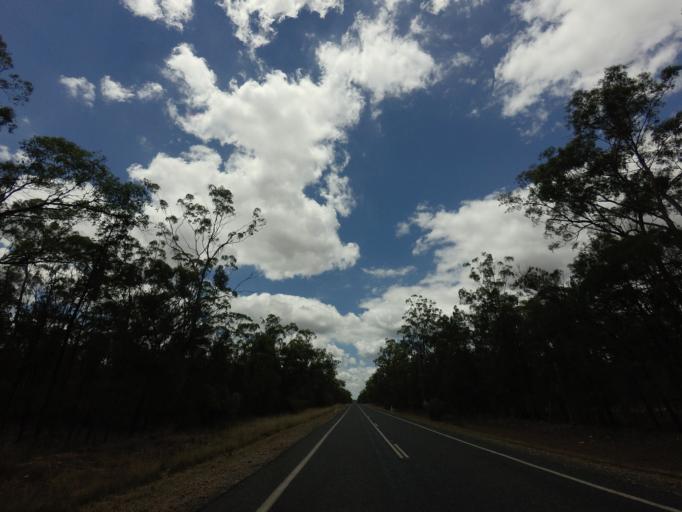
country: AU
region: Queensland
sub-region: Goondiwindi
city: Goondiwindi
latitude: -28.0190
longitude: 150.8577
